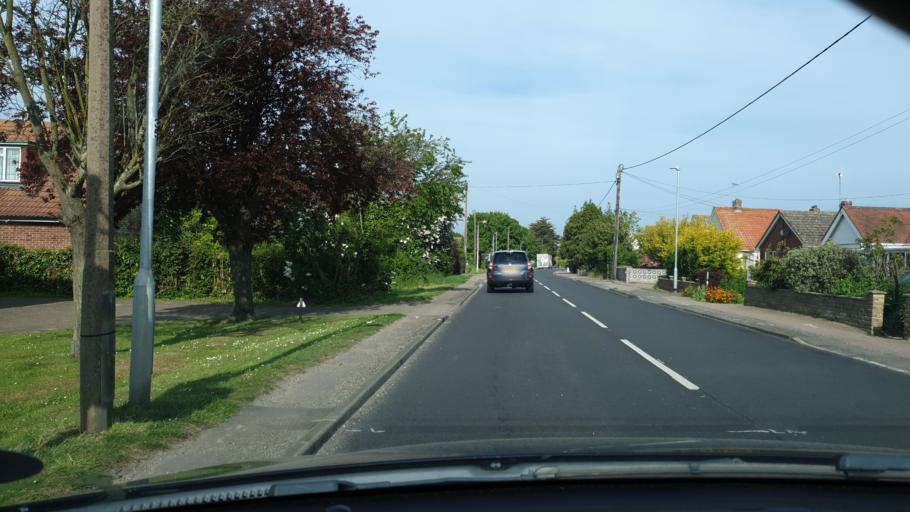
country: GB
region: England
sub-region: Essex
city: Frinton-on-Sea
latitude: 51.8446
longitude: 1.2058
